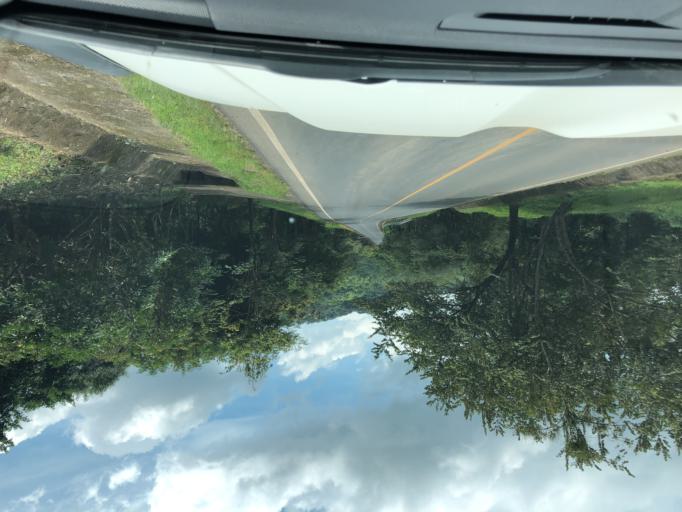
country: NI
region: Chontales
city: Villa Sandino
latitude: 12.0592
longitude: -85.0417
